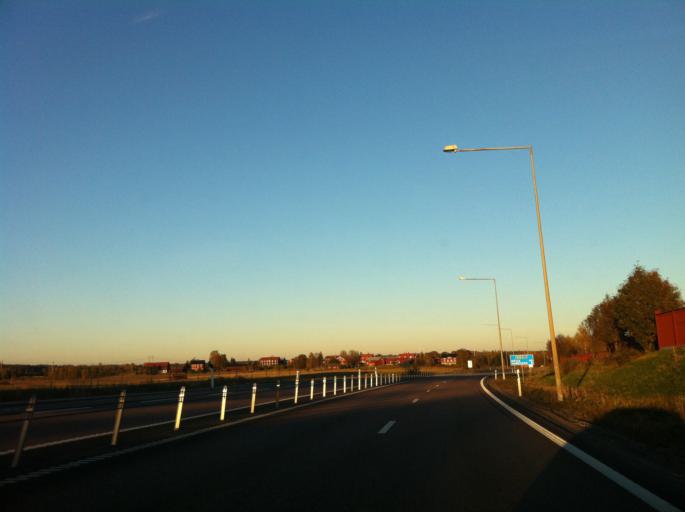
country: SE
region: Gaevleborg
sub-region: Sandvikens Kommun
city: Jarbo
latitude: 60.6065
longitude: 16.5931
